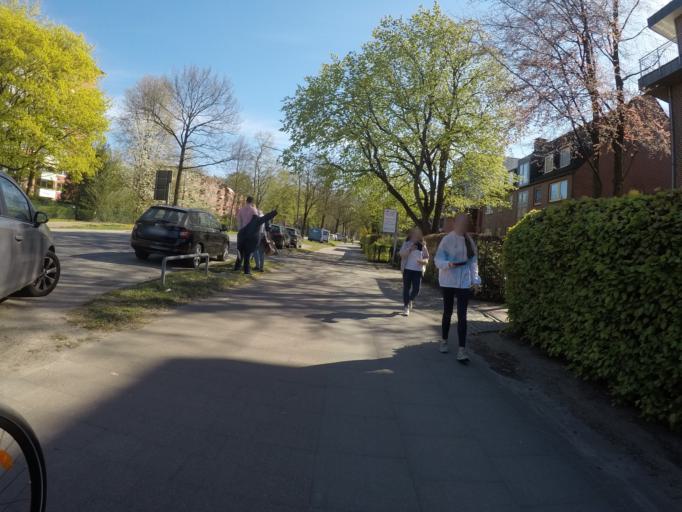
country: DE
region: Hamburg
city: Eidelstedt
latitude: 53.6319
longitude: 9.9106
